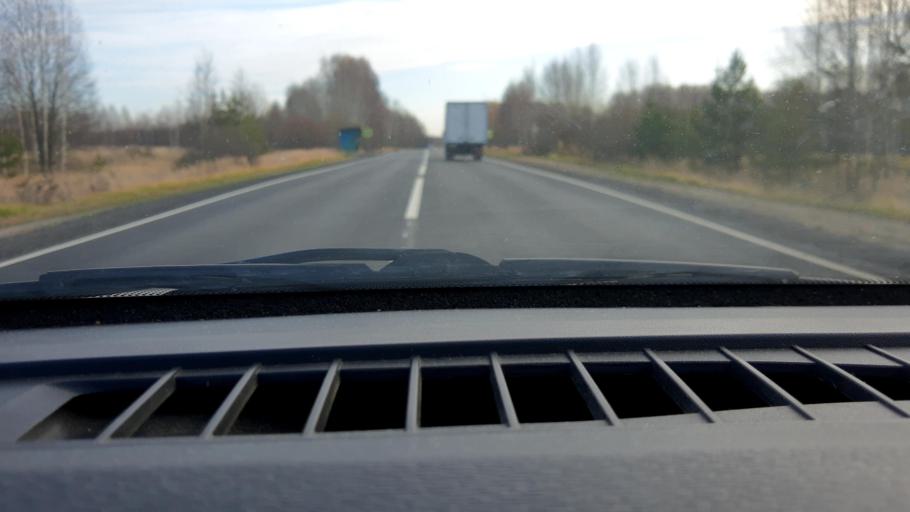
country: RU
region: Nizjnij Novgorod
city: Novaya Balakhna
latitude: 56.5918
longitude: 43.6585
